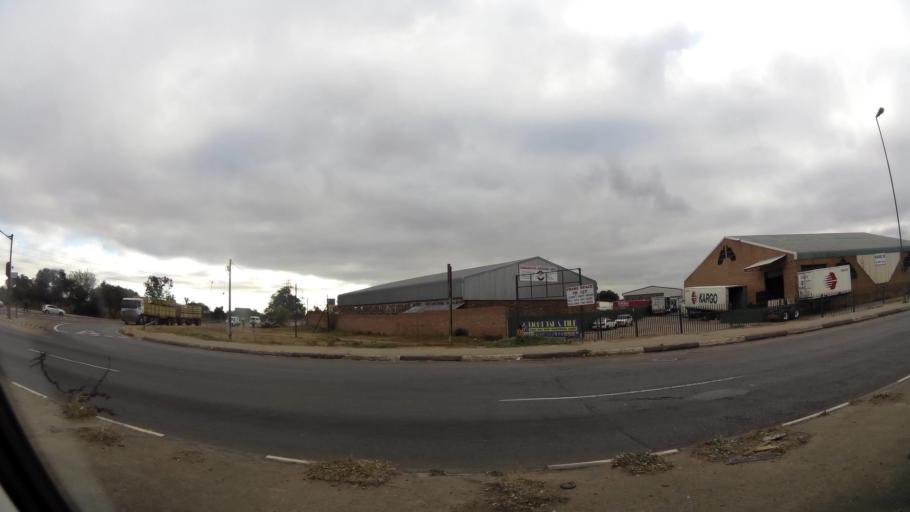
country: ZA
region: Limpopo
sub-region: Capricorn District Municipality
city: Polokwane
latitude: -23.8878
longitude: 29.4302
